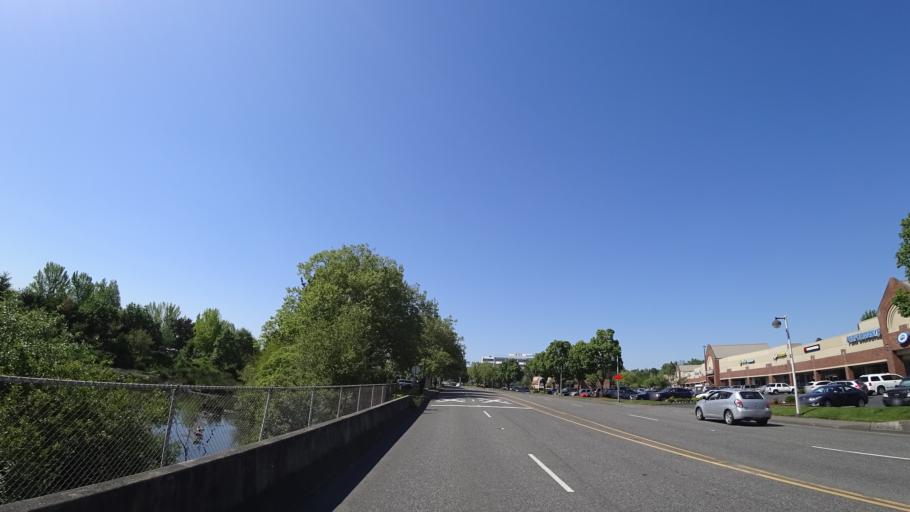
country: US
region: Oregon
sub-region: Washington County
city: Beaverton
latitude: 45.4914
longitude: -122.8059
